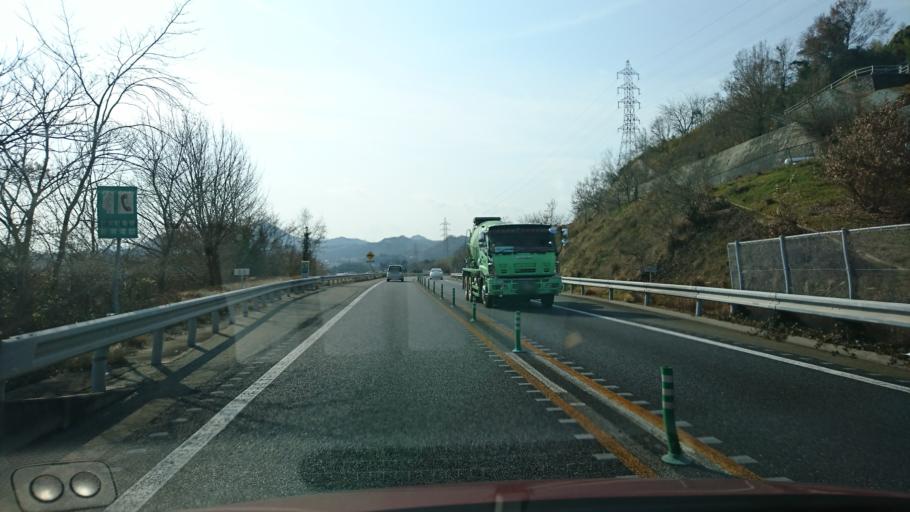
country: JP
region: Hiroshima
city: Onomichi
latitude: 34.4045
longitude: 133.2123
